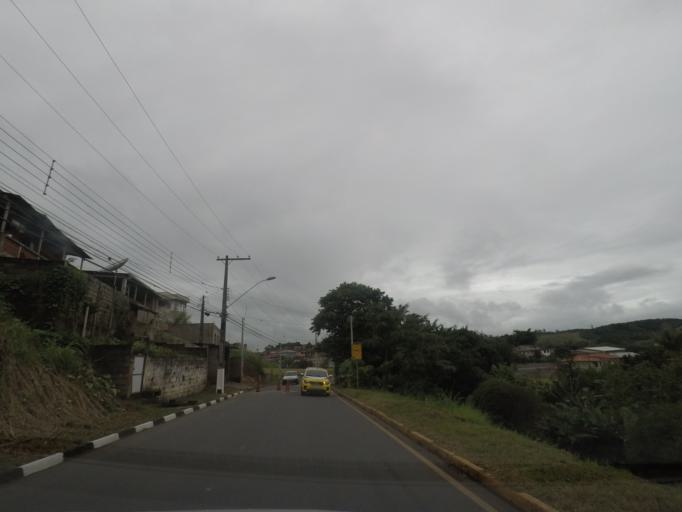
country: BR
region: Sao Paulo
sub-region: Cajati
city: Cajati
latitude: -24.7215
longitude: -48.1045
